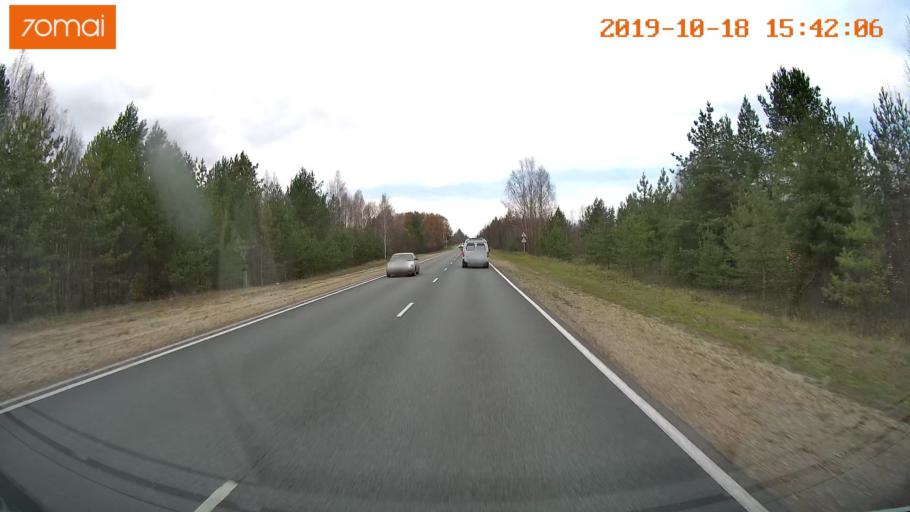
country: RU
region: Vladimir
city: Golovino
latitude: 55.9521
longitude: 40.5731
